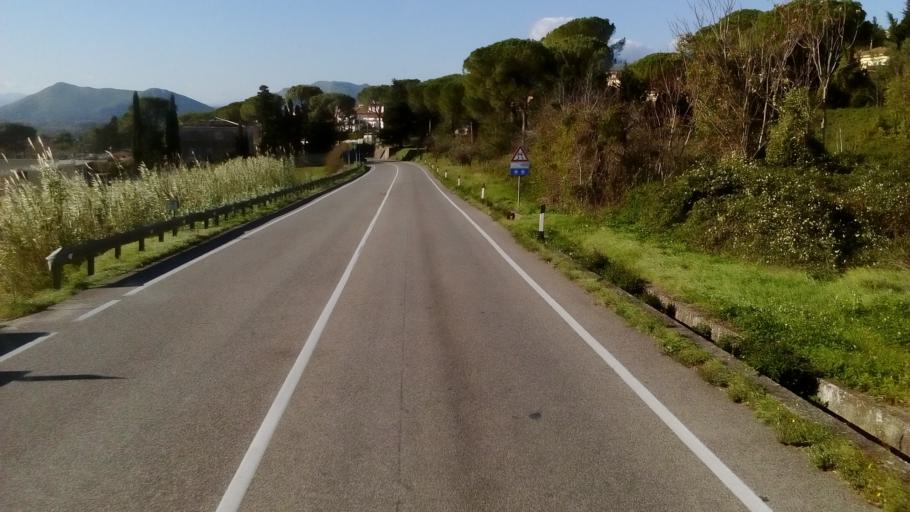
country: IT
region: Campania
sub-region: Provincia di Caserta
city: San Pietro Infine
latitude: 41.4441
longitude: 13.9652
